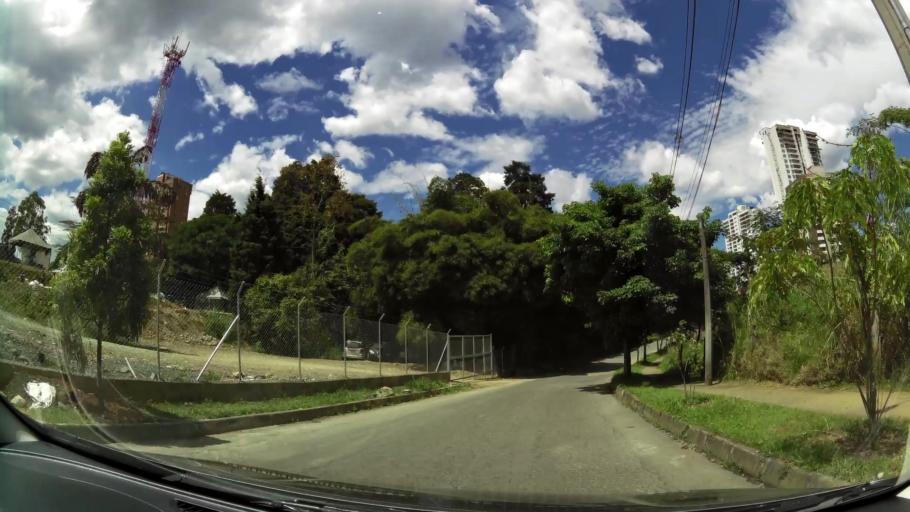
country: CO
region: Antioquia
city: La Estrella
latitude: 6.1599
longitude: -75.6322
